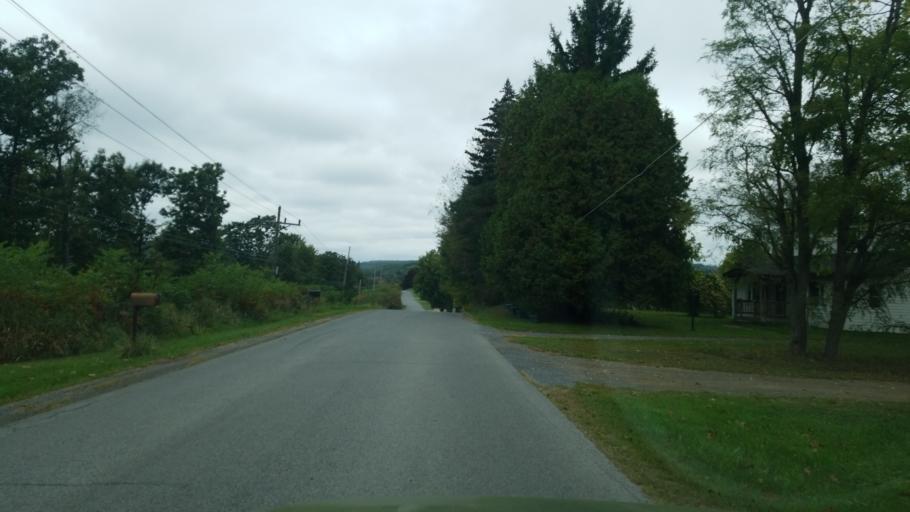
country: US
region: Pennsylvania
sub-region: Clearfield County
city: Curwensville
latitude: 40.9688
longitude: -78.5077
